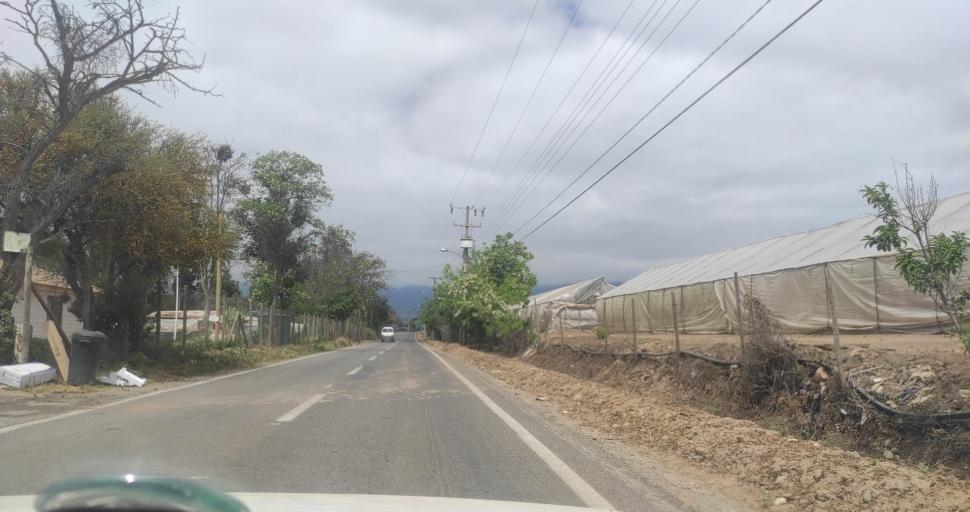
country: CL
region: Valparaiso
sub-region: Provincia de Marga Marga
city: Limache
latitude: -33.0206
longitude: -71.2299
